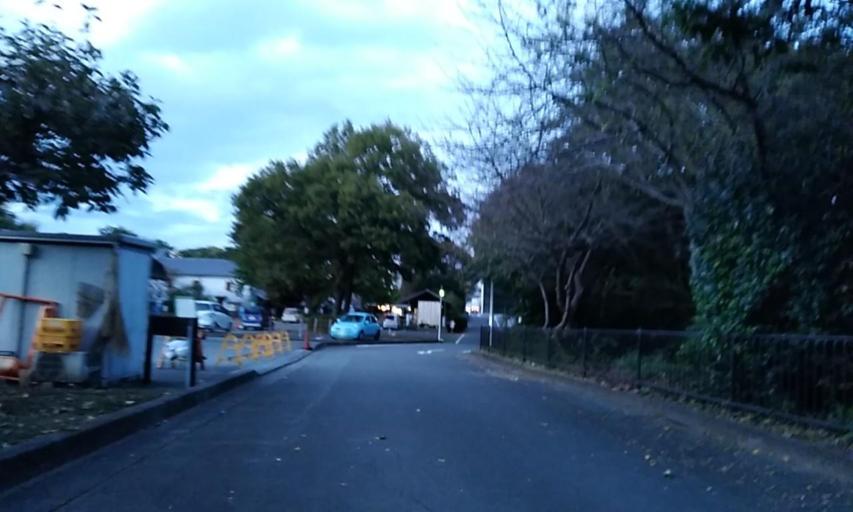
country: JP
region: Shizuoka
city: Mishima
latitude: 35.1061
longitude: 138.9028
